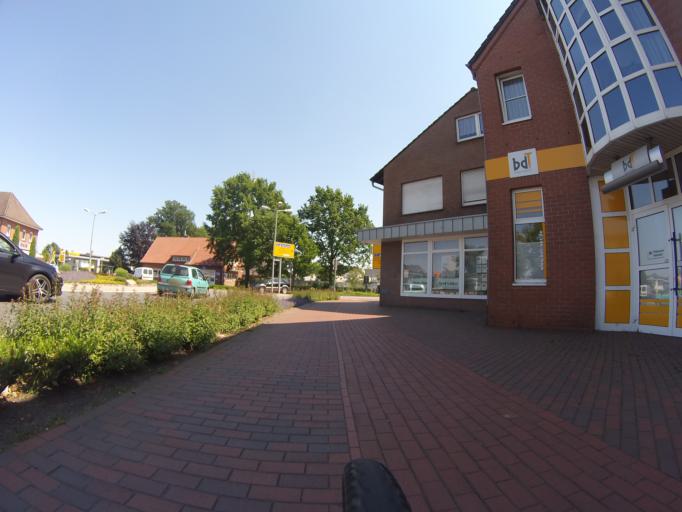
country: DE
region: Lower Saxony
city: Emlichheim
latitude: 52.6068
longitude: 6.8532
